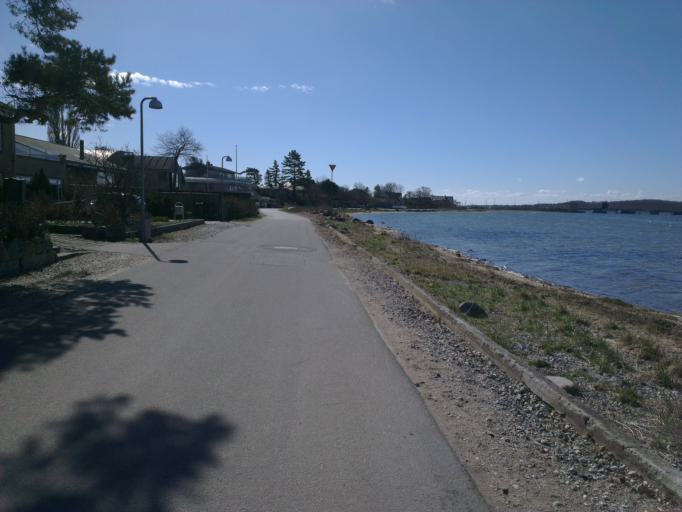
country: DK
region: Capital Region
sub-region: Frederikssund Kommune
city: Frederikssund
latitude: 55.8488
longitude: 12.0443
